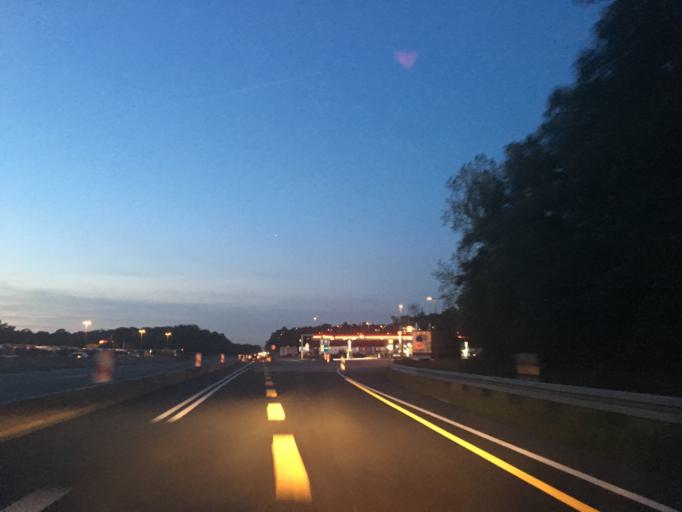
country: DE
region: Hesse
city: Lorsch
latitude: 49.6414
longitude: 8.5533
